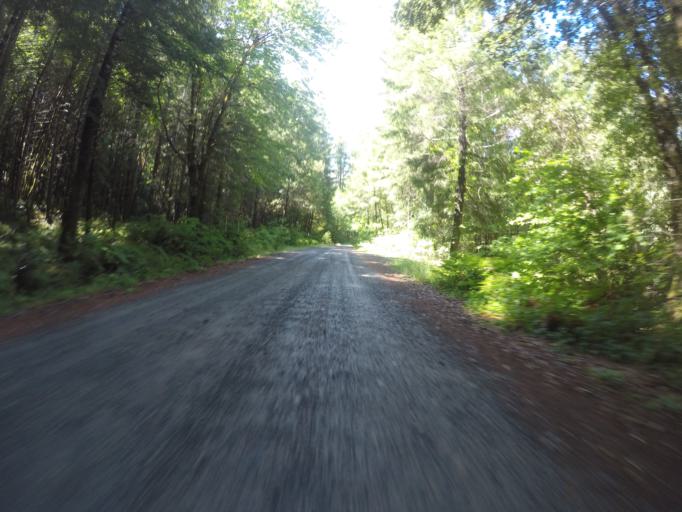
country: US
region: California
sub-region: Del Norte County
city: Bertsch-Oceanview
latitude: 41.6898
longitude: -123.9056
